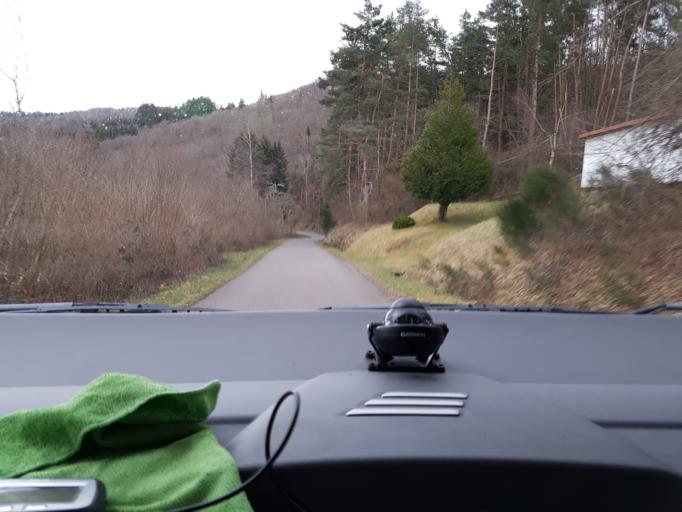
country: FR
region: Auvergne
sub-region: Departement du Puy-de-Dome
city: Chapdes-Beaufort
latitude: 45.8614
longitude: 2.8353
